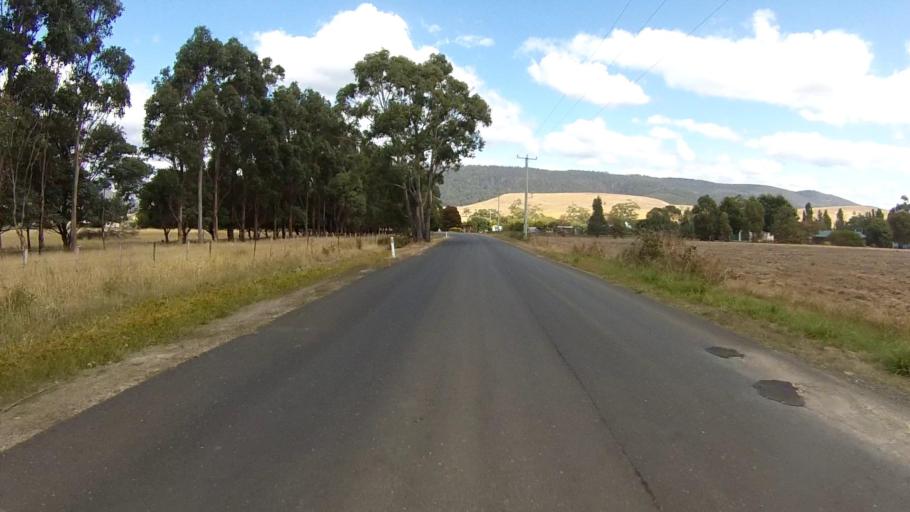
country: AU
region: Tasmania
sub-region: Derwent Valley
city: New Norfolk
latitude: -42.7503
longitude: 146.9738
